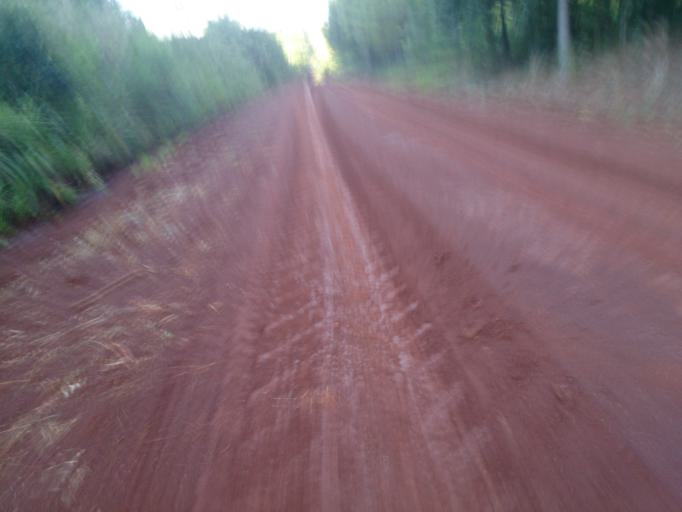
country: AR
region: Misiones
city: Florentino Ameghino
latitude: -27.5676
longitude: -55.1679
